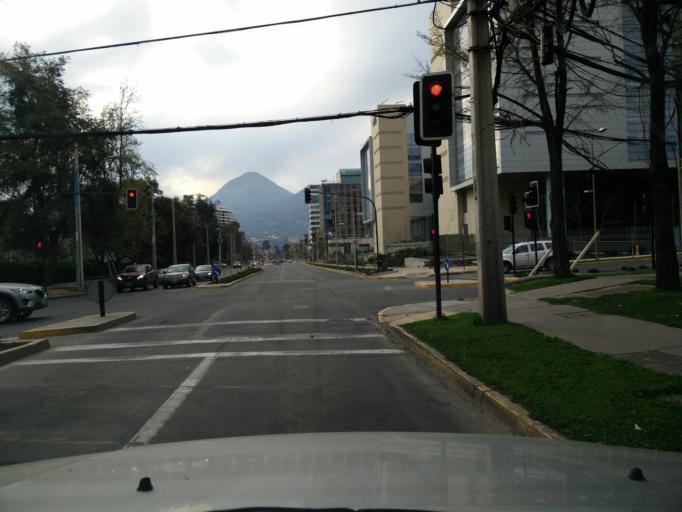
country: CL
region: Santiago Metropolitan
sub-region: Provincia de Santiago
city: Villa Presidente Frei, Nunoa, Santiago, Chile
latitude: -33.3862
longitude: -70.5310
